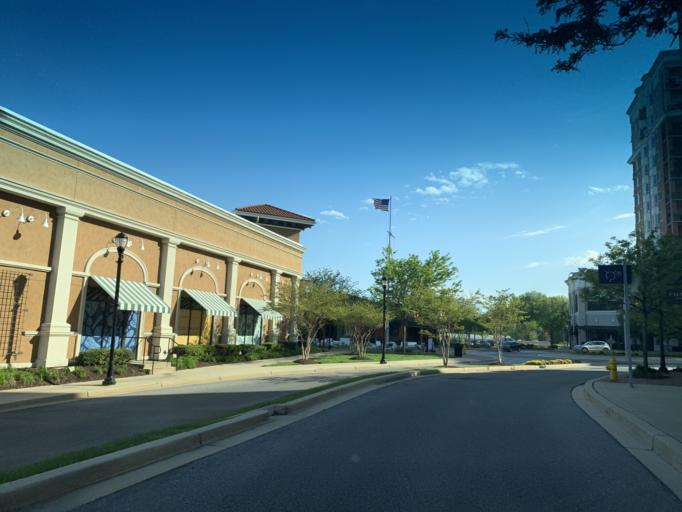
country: US
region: Maryland
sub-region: Anne Arundel County
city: Parole
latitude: 38.9807
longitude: -76.5385
